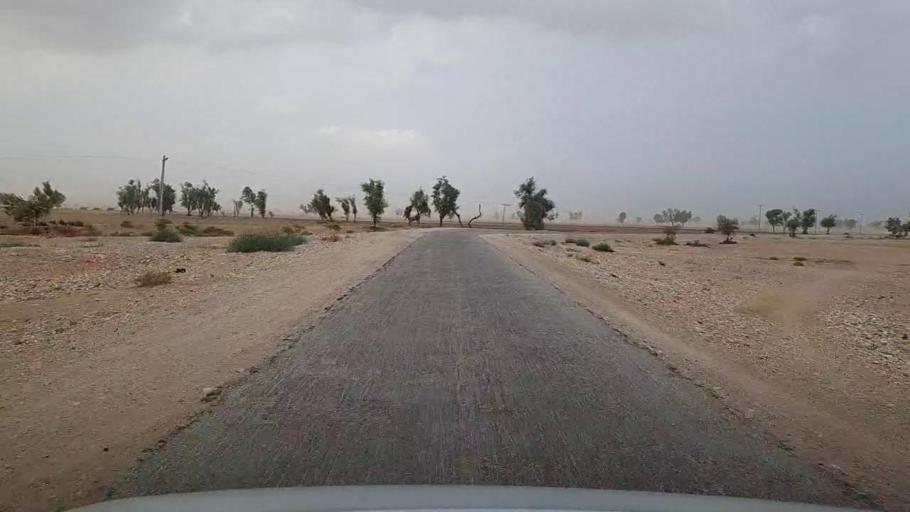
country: PK
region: Sindh
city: Sehwan
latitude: 26.3189
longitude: 67.7300
